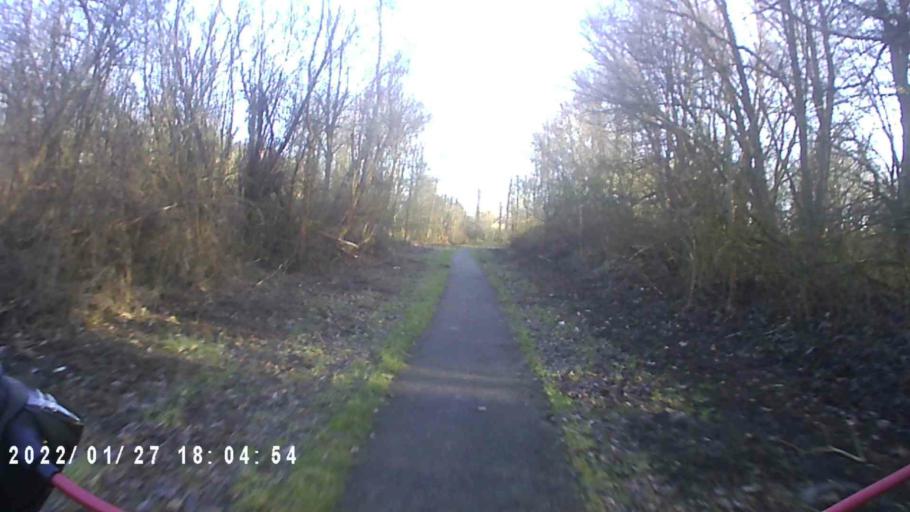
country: NL
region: Friesland
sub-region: Gemeente Dongeradeel
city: Anjum
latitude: 53.4065
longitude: 6.2164
